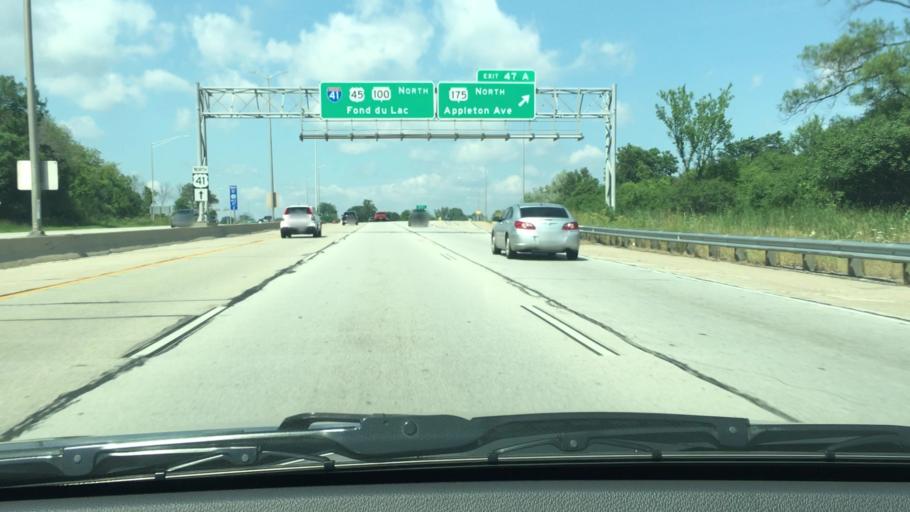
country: US
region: Wisconsin
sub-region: Waukesha County
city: Butler
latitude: 43.1280
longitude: -88.0560
